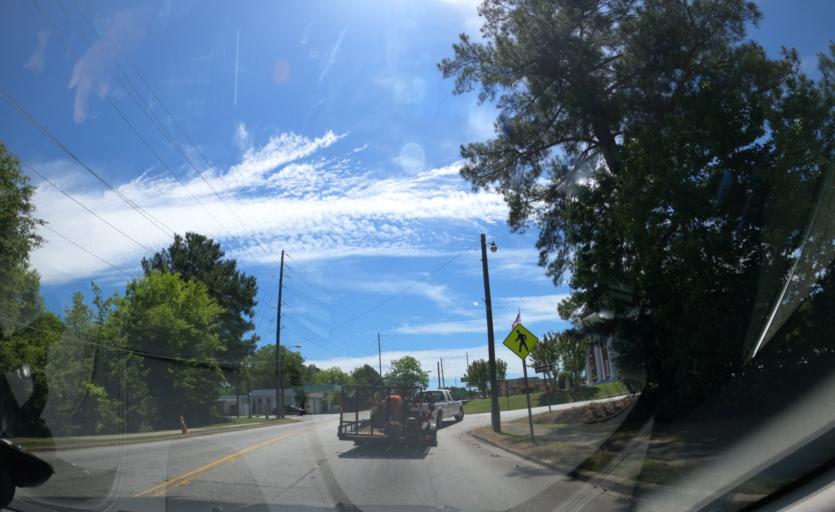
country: US
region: South Carolina
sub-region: McCormick County
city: McCormick
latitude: 33.9111
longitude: -82.2948
